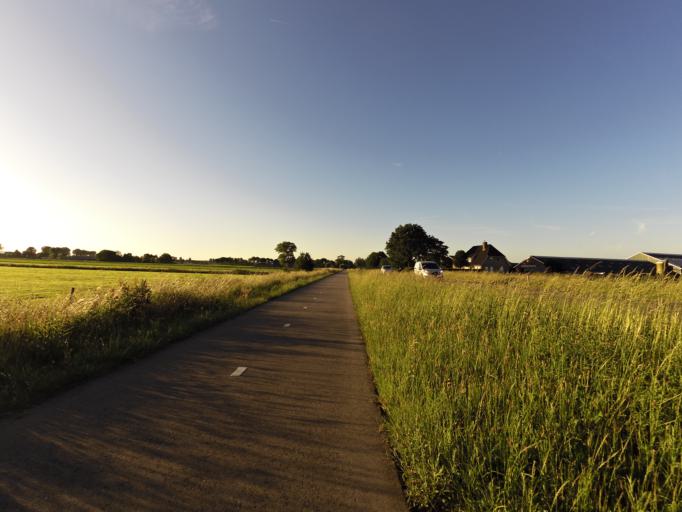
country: NL
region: Gelderland
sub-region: Gemeente Zevenaar
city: Zevenaar
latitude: 51.9573
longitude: 6.0829
